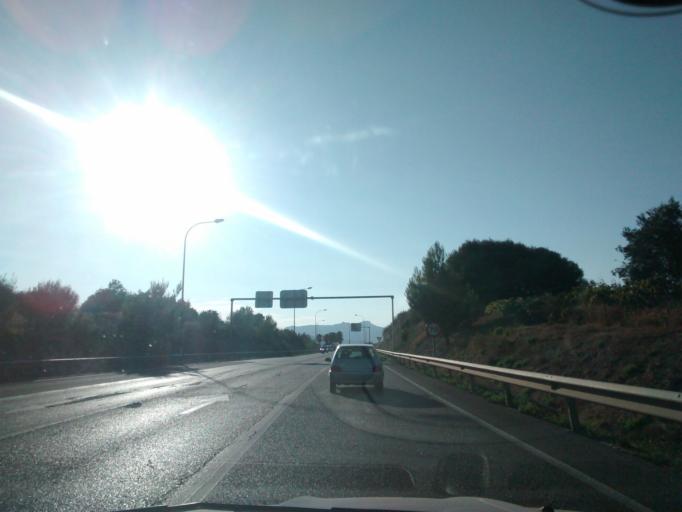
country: ES
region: Balearic Islands
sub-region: Illes Balears
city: Alcudia
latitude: 39.8431
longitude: 3.0973
